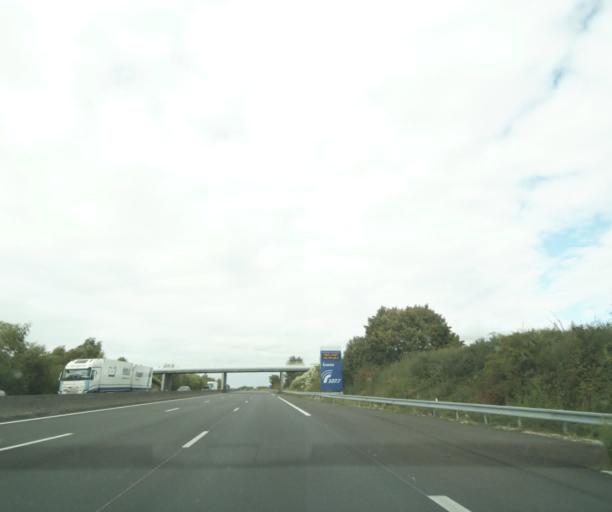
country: FR
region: Centre
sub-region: Departement d'Eure-et-Loir
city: Janville
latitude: 48.2391
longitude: 1.8509
